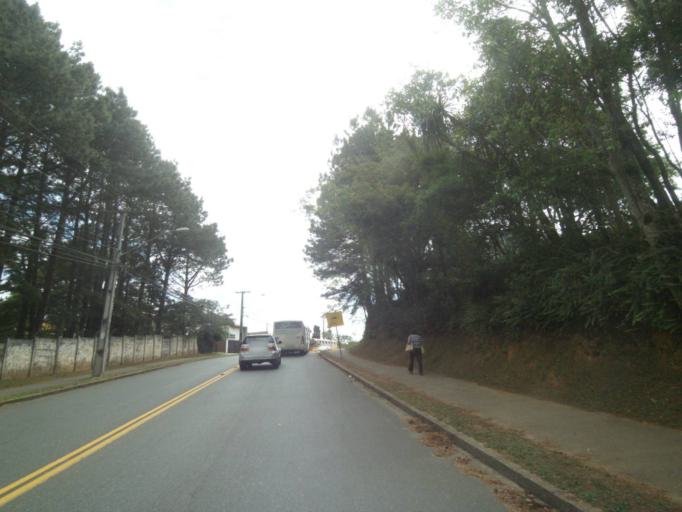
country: BR
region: Parana
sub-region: Curitiba
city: Curitiba
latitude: -25.3935
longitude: -49.2909
